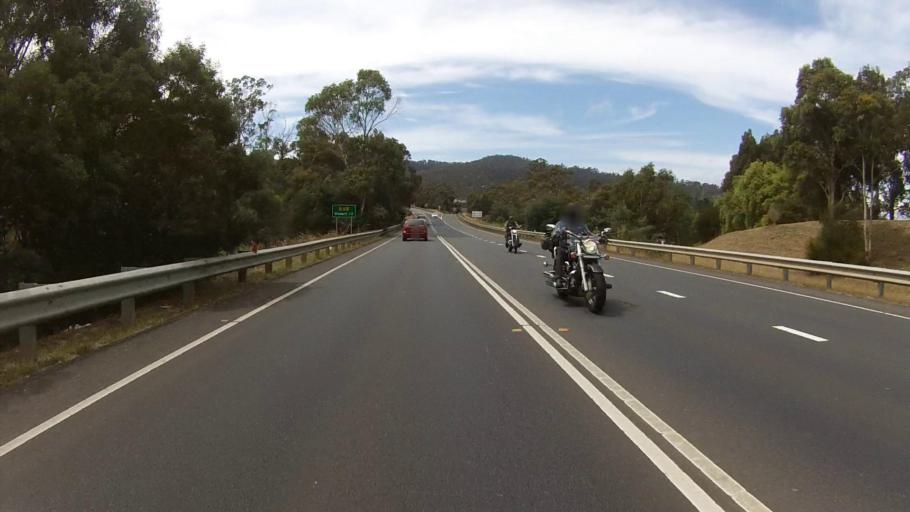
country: AU
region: Tasmania
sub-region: Kingborough
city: Kingston
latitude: -42.9729
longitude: 147.3061
